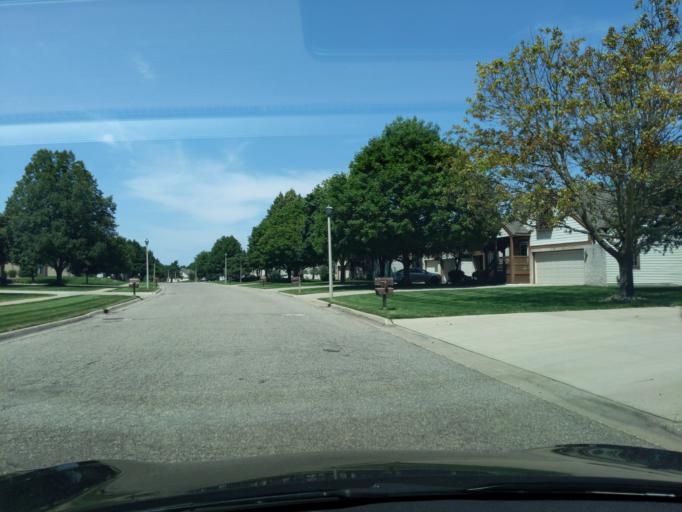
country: US
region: Michigan
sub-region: Eaton County
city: Waverly
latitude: 42.7455
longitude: -84.6472
